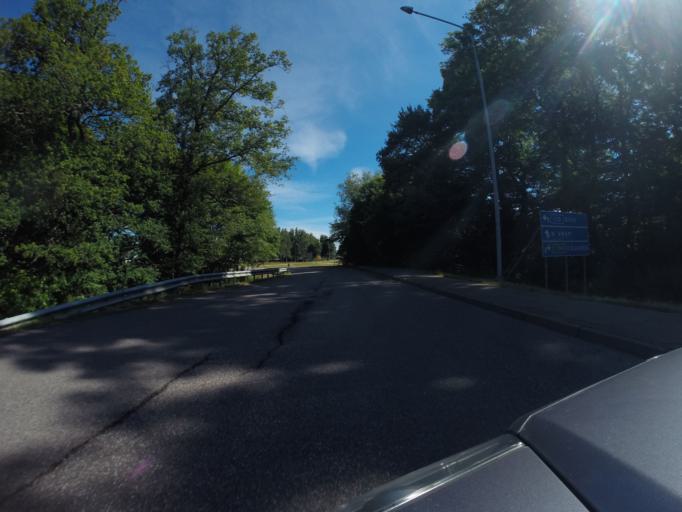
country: SE
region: Skane
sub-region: Bjuvs Kommun
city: Billesholm
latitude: 56.0597
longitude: 12.9778
